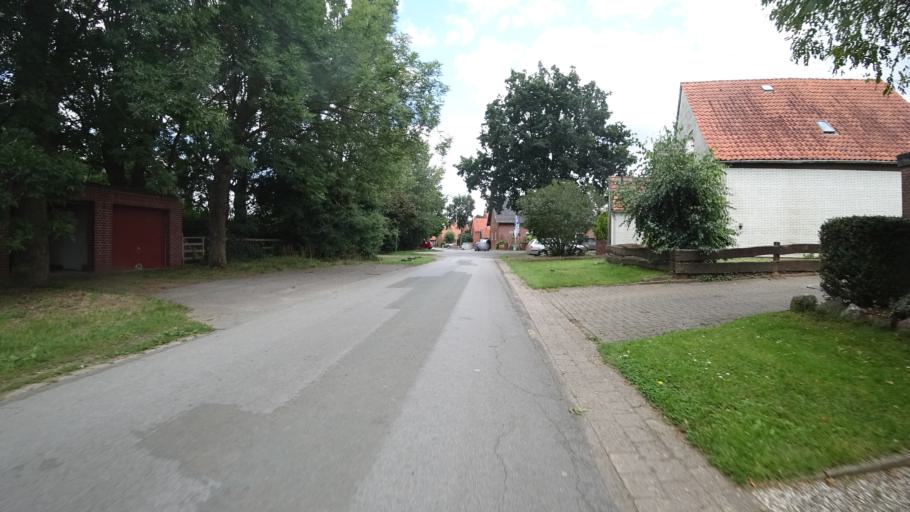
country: DE
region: Lower Saxony
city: Raddestorf
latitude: 52.4142
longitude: 9.0074
